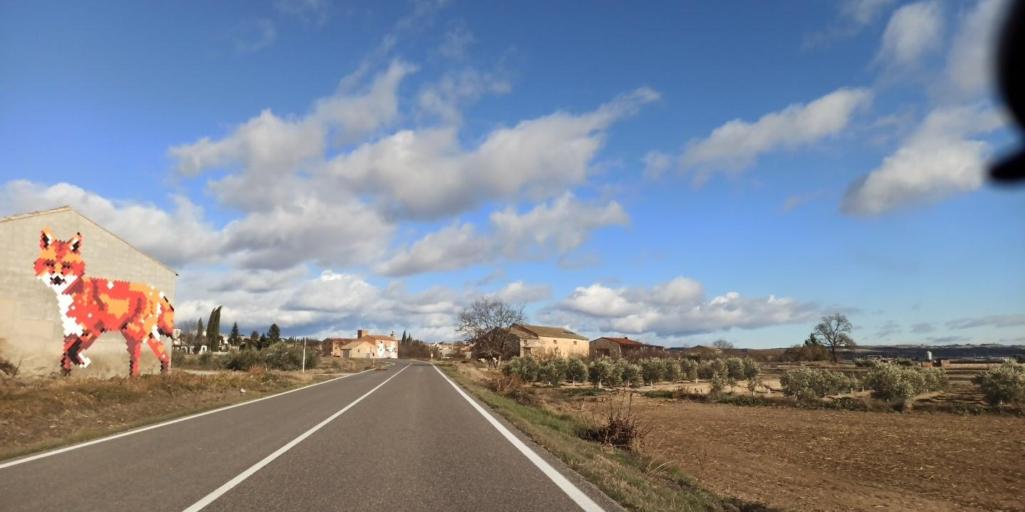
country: ES
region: Catalonia
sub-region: Provincia de Lleida
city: Penelles
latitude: 41.7535
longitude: 0.9579
